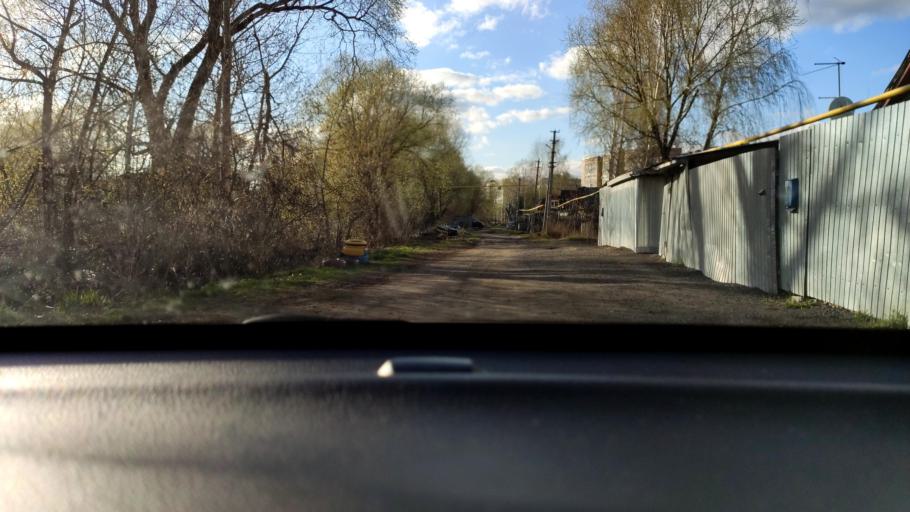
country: RU
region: Tatarstan
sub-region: Gorod Kazan'
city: Kazan
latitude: 55.8188
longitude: 49.0709
